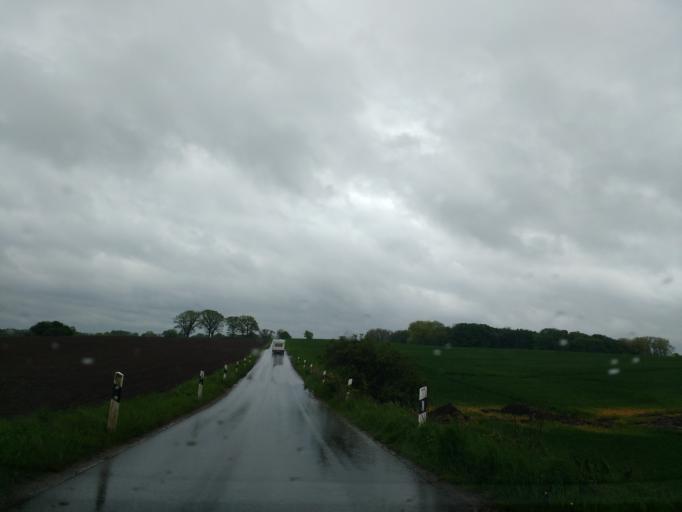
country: DE
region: Schleswig-Holstein
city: Loose
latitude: 54.5091
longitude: 9.9201
